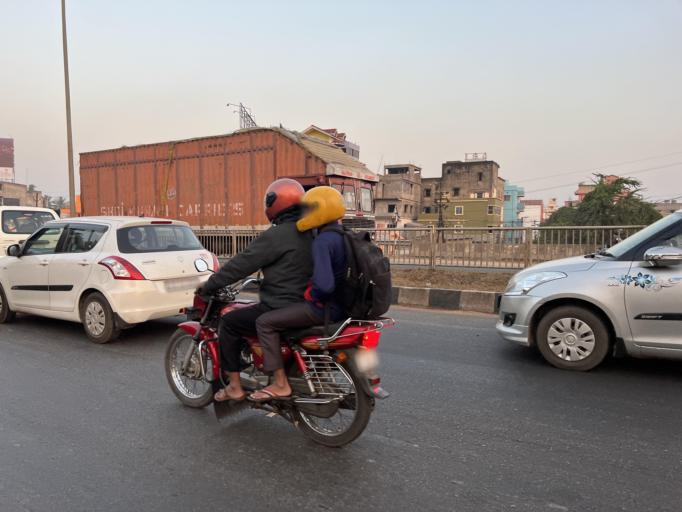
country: IN
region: Odisha
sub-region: Khordha
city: Bhubaneshwar
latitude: 20.3071
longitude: 85.8699
